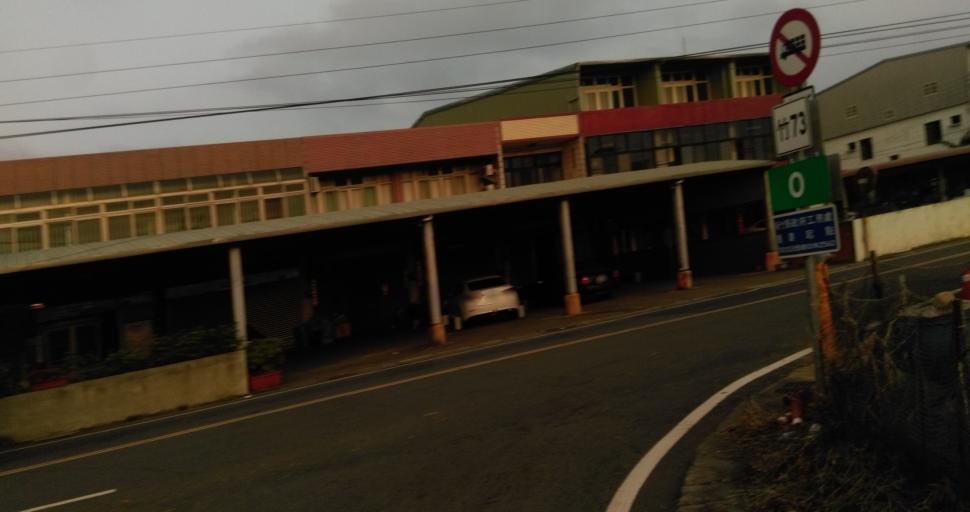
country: TW
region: Taiwan
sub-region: Hsinchu
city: Zhubei
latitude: 24.8766
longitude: 120.9546
